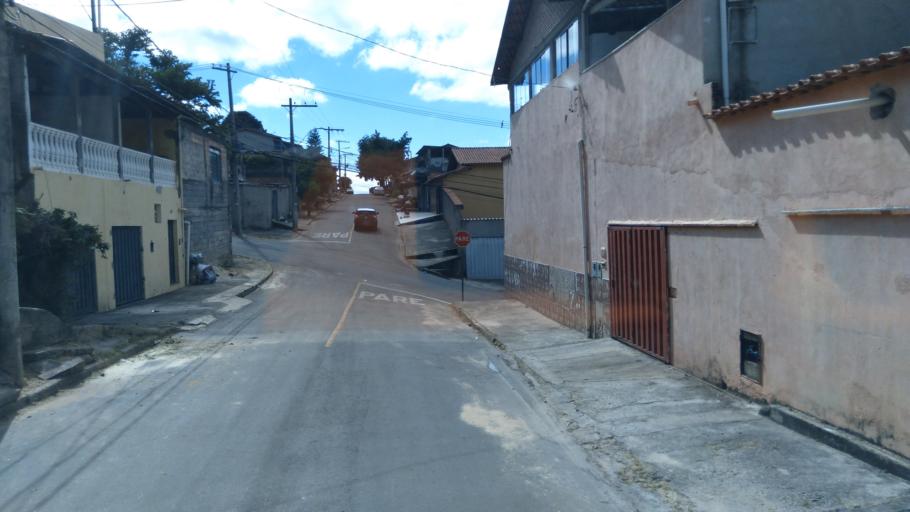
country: BR
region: Minas Gerais
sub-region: Belo Horizonte
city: Belo Horizonte
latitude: -19.8594
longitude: -43.9094
